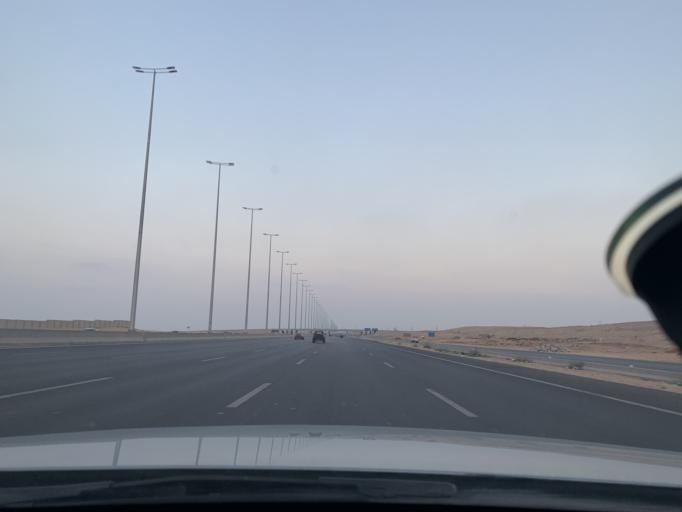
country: EG
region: Muhafazat al Qalyubiyah
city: Al Khankah
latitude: 30.0925
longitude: 31.4970
